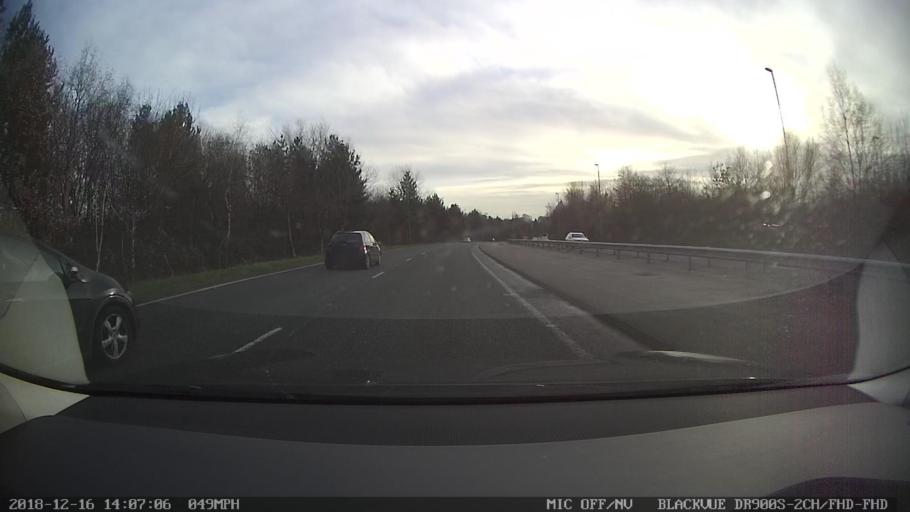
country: GB
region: England
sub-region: Borough of Stockport
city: Cheadle Hulme
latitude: 53.3763
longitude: -2.2125
